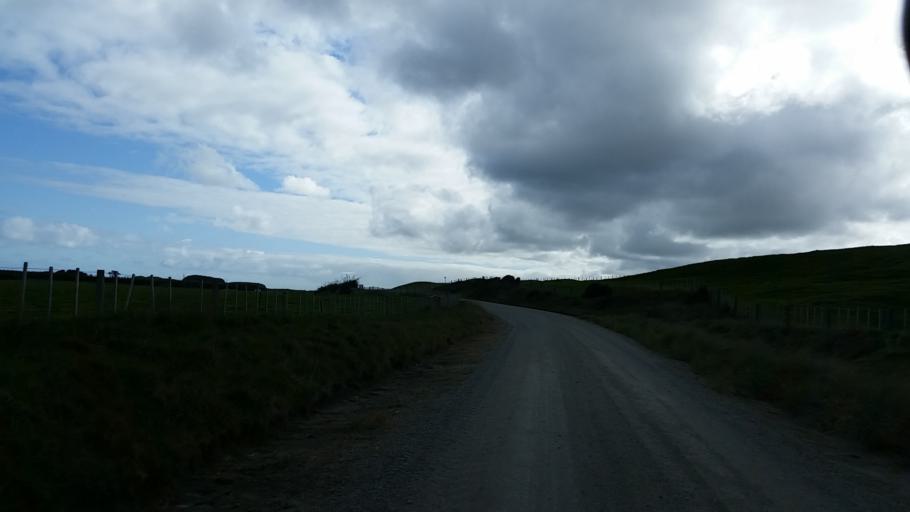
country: NZ
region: Taranaki
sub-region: South Taranaki District
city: Patea
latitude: -39.7929
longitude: 174.5851
